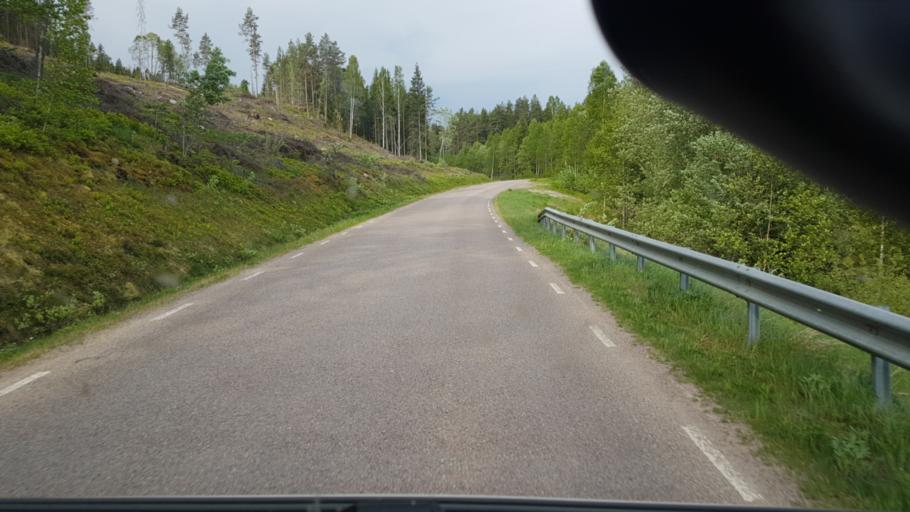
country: SE
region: Vaermland
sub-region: Arvika Kommun
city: Arvika
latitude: 59.5476
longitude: 12.5354
